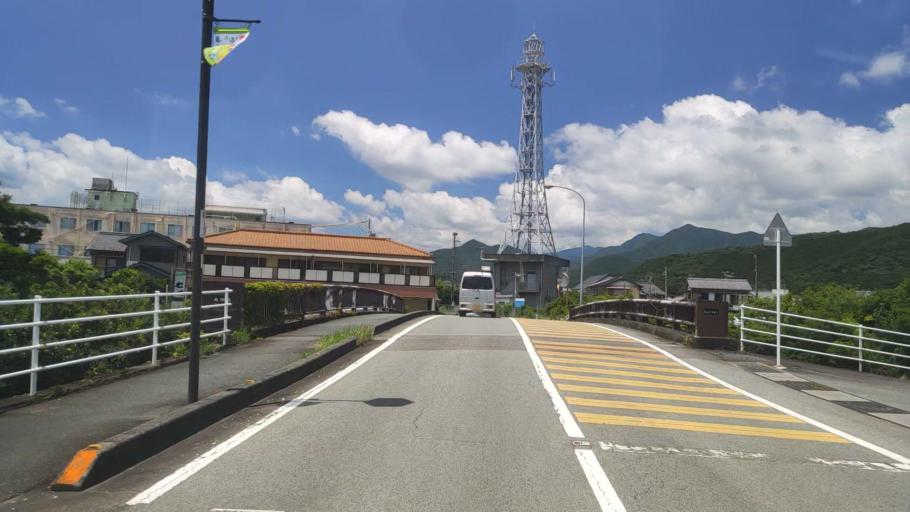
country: JP
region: Mie
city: Owase
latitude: 34.2081
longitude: 136.3389
